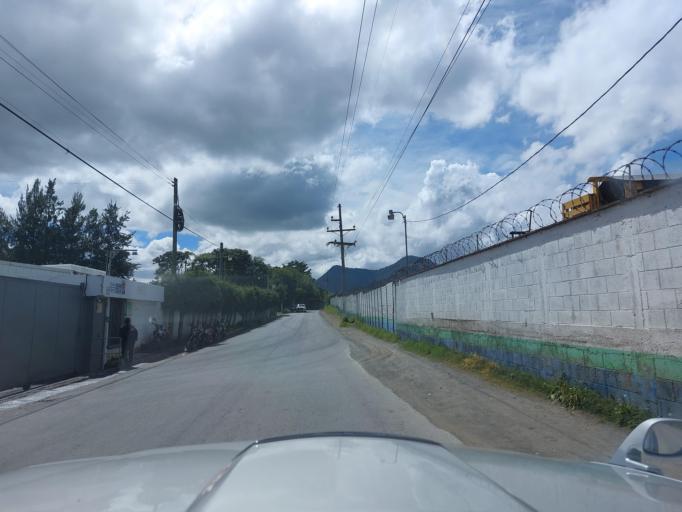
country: GT
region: Chimaltenango
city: Parramos
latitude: 14.6097
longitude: -90.8132
